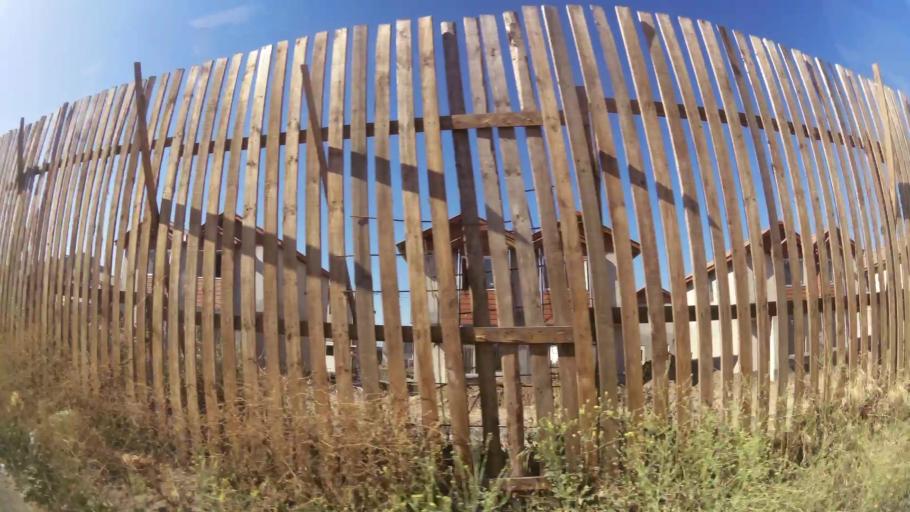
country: CL
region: Santiago Metropolitan
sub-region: Provincia de Maipo
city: San Bernardo
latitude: -33.6086
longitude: -70.6800
